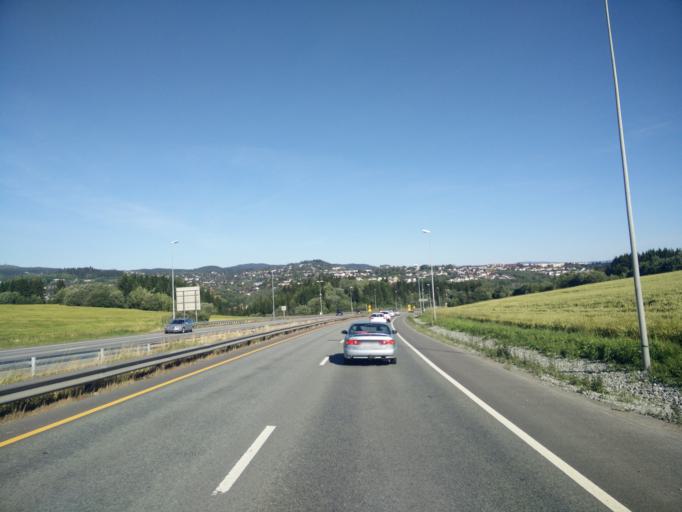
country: NO
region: Sor-Trondelag
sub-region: Trondheim
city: Trondheim
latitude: 63.3764
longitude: 10.3762
